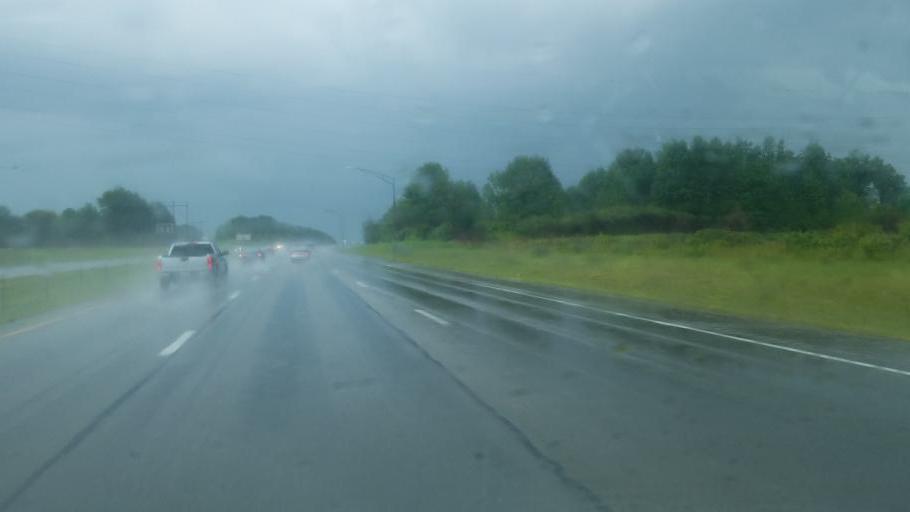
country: US
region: Ohio
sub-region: Trumbull County
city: Morgandale
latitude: 41.2771
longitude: -80.7972
